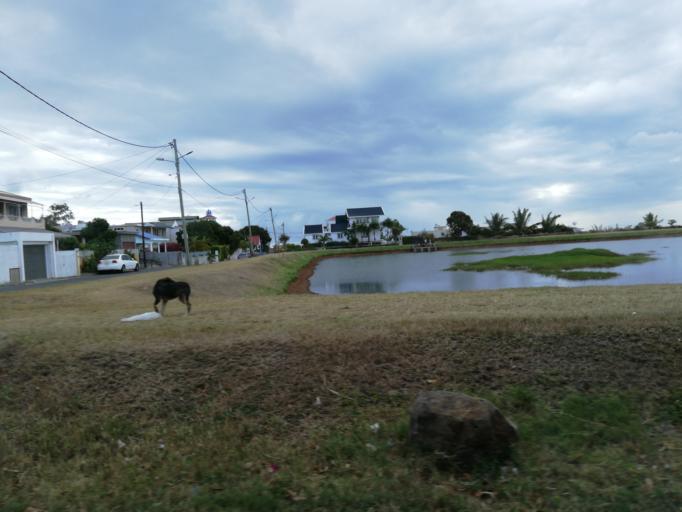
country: MU
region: Plaines Wilhems
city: Quatre Bornes
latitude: -20.2362
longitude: 57.4547
